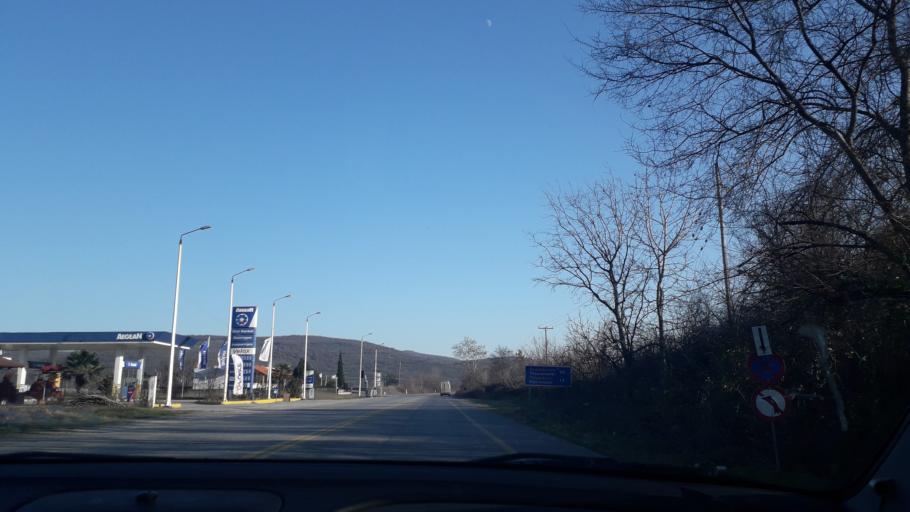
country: GR
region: Central Macedonia
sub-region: Nomos Pellis
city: Apsalos
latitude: 40.8864
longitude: 22.0732
